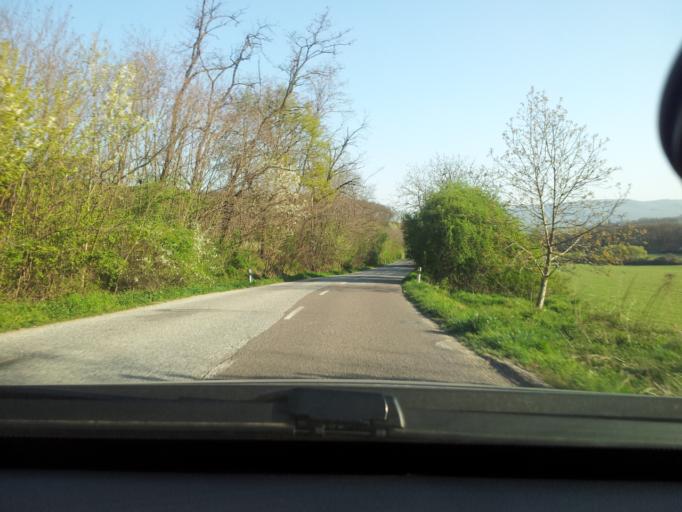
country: SK
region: Nitriansky
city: Tlmace
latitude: 48.2917
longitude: 18.4504
